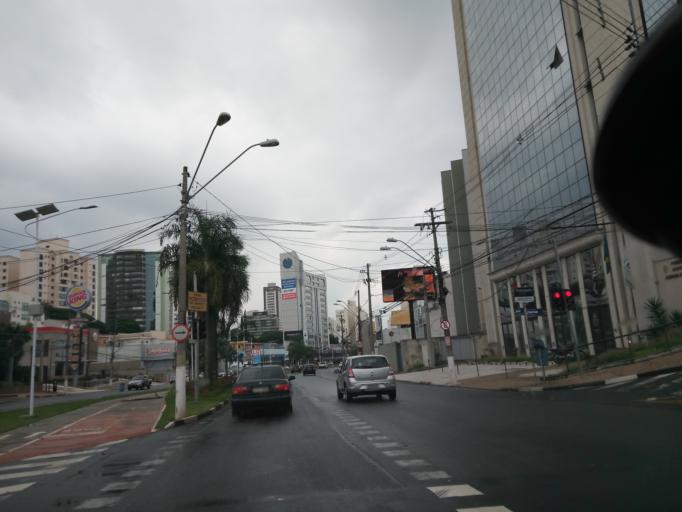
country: BR
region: Sao Paulo
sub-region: Campinas
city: Campinas
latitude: -22.8943
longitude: -47.0473
